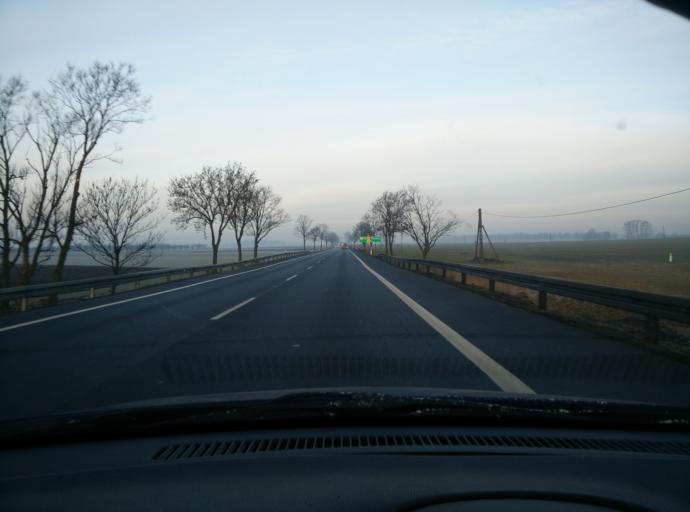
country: PL
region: Greater Poland Voivodeship
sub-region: Powiat poznanski
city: Kornik
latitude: 52.2423
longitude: 17.1385
